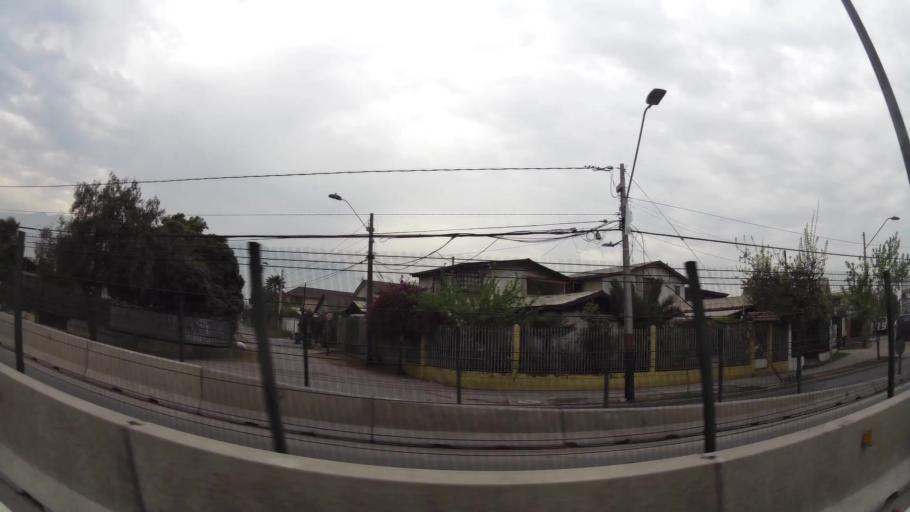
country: CL
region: Santiago Metropolitan
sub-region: Provincia de Santiago
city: La Pintana
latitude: -33.5277
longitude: -70.6031
